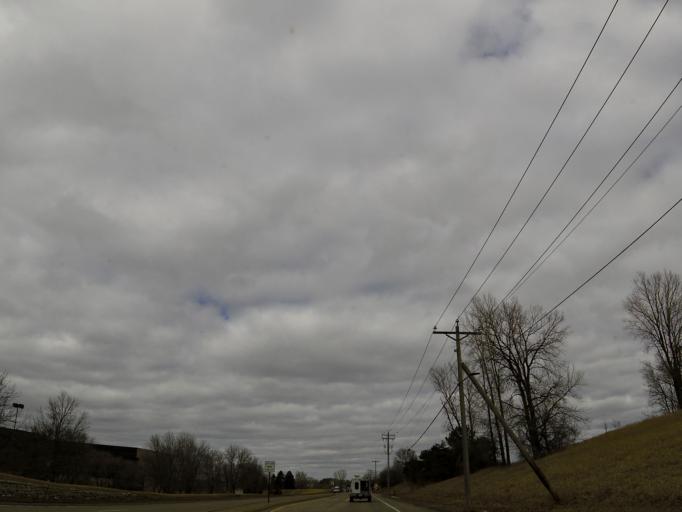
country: US
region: Minnesota
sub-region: Washington County
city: Woodbury
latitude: 44.9438
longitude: -92.9543
